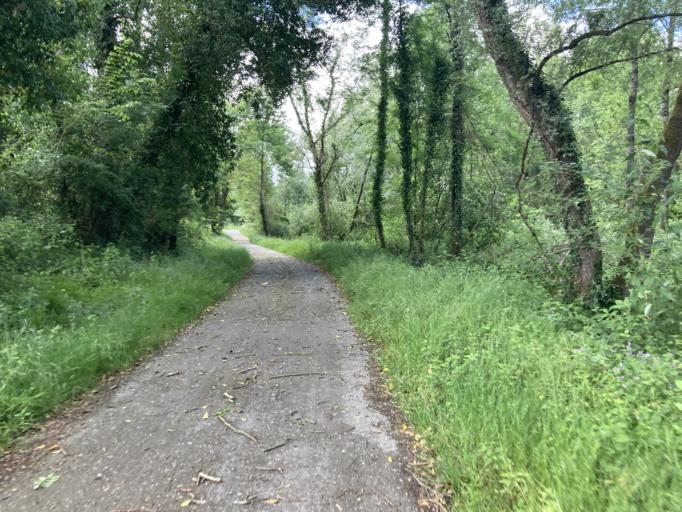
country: FR
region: Aquitaine
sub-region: Departement des Pyrenees-Atlantiques
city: Denguin
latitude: 43.3534
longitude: -0.5161
